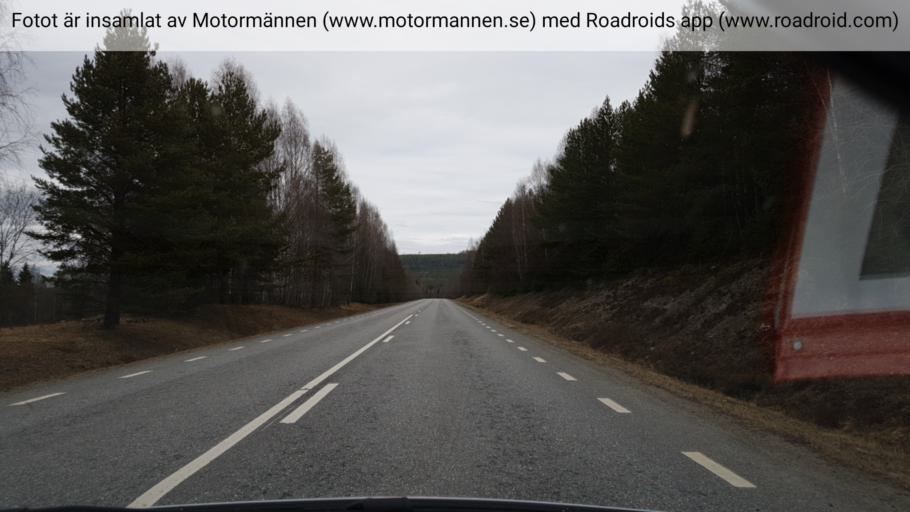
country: SE
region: Vaesternorrland
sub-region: Solleftea Kommun
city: Solleftea
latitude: 63.2759
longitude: 17.2121
